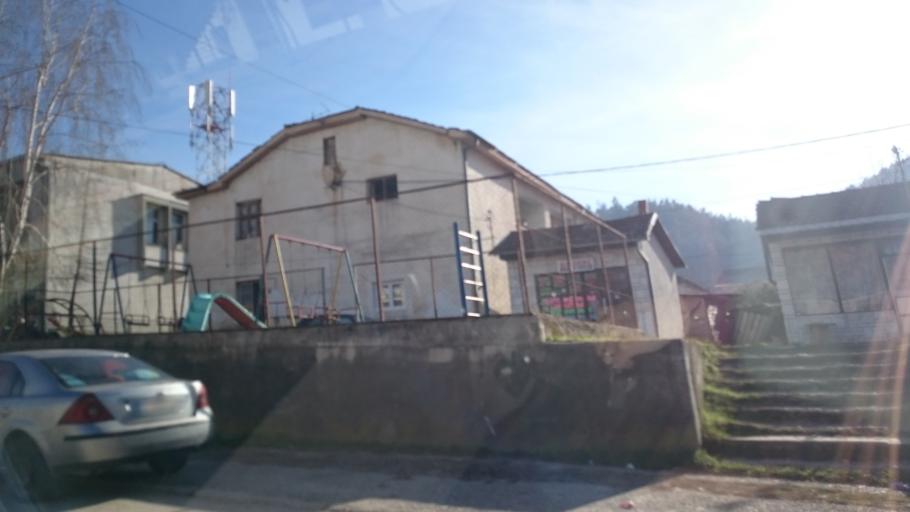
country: MK
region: Makedonski Brod
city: Makedonski Brod
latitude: 41.5074
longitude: 21.2187
